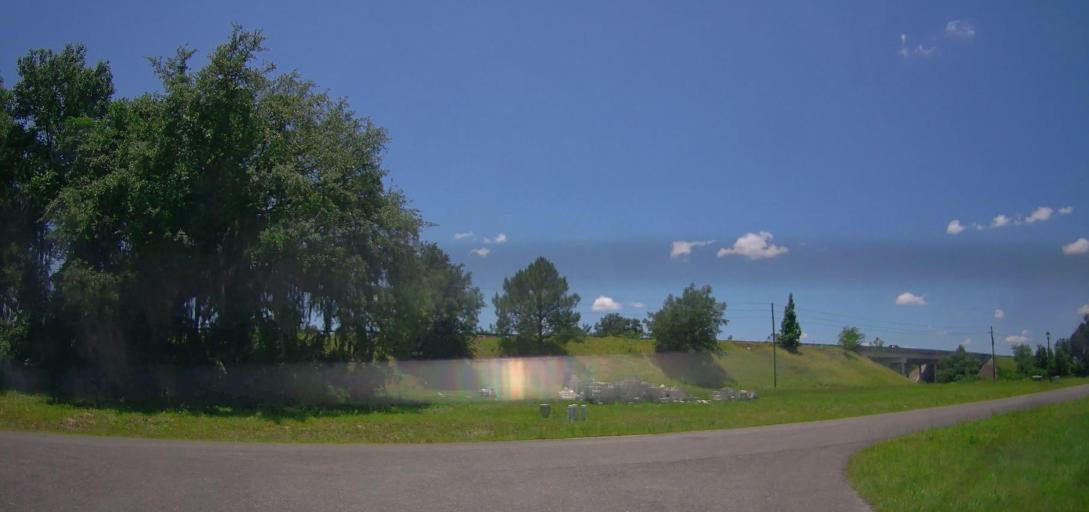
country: US
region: Florida
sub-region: Marion County
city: Belleview
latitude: 29.0889
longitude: -82.0747
